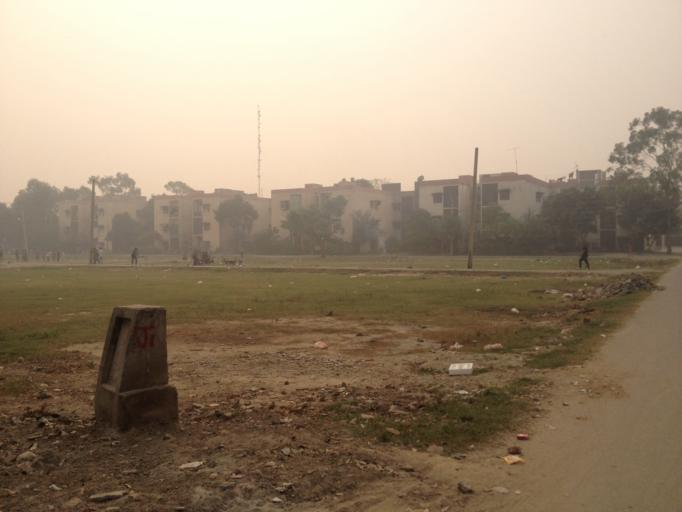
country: PK
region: Punjab
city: Lahore
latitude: 31.4653
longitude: 74.2999
